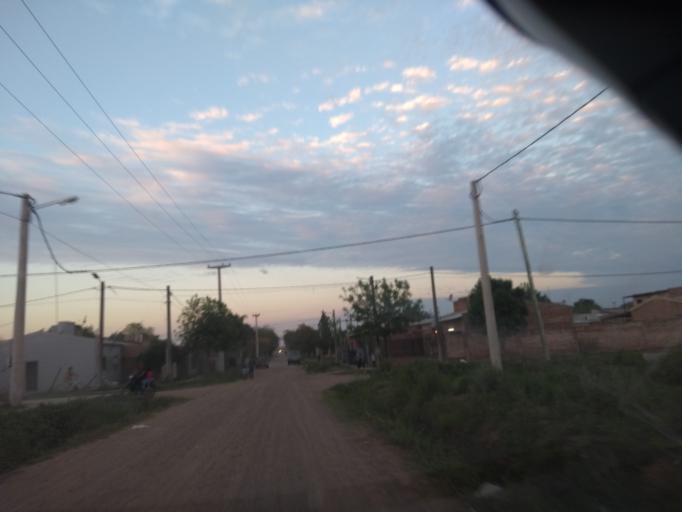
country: AR
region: Chaco
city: Fontana
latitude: -27.4070
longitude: -59.0483
